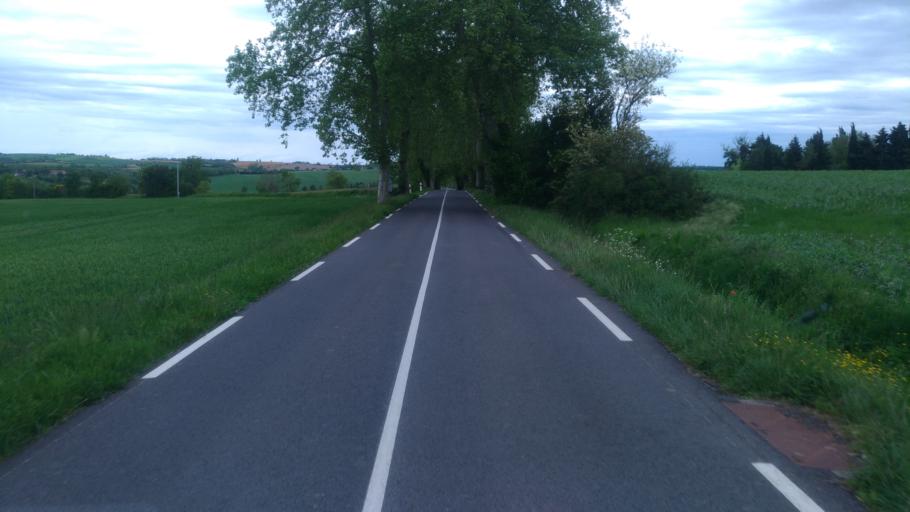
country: FR
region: Midi-Pyrenees
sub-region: Departement de la Haute-Garonne
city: Avignonet-Lauragais
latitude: 43.4379
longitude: 1.7807
